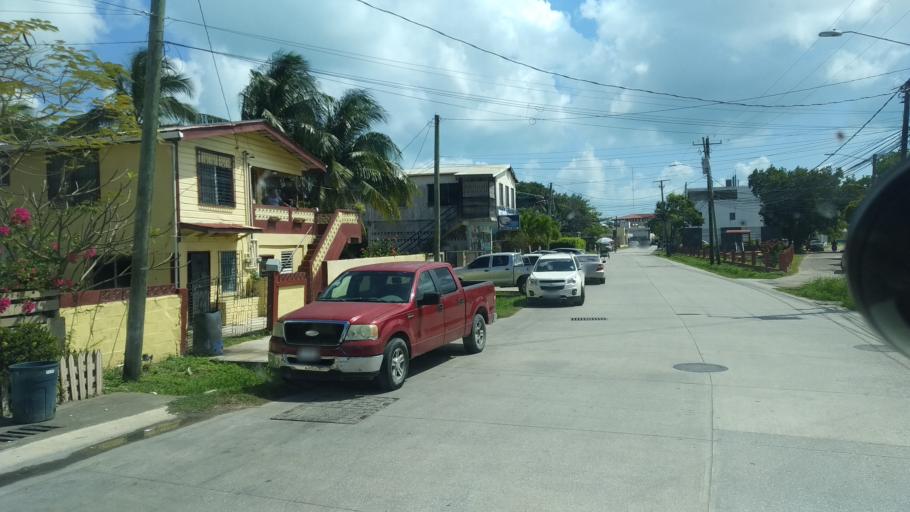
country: BZ
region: Belize
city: Belize City
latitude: 17.5044
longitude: -88.1903
